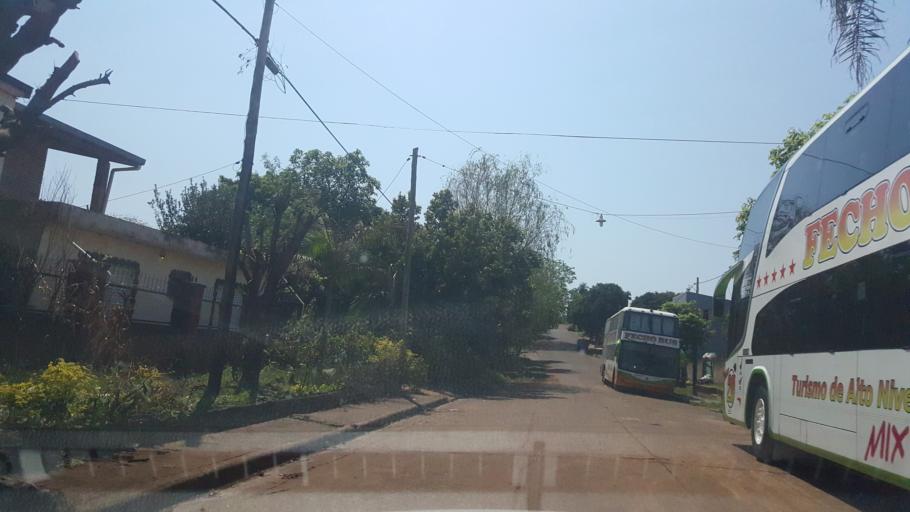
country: AR
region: Misiones
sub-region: Departamento de Capital
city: Posadas
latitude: -27.4027
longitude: -55.9110
